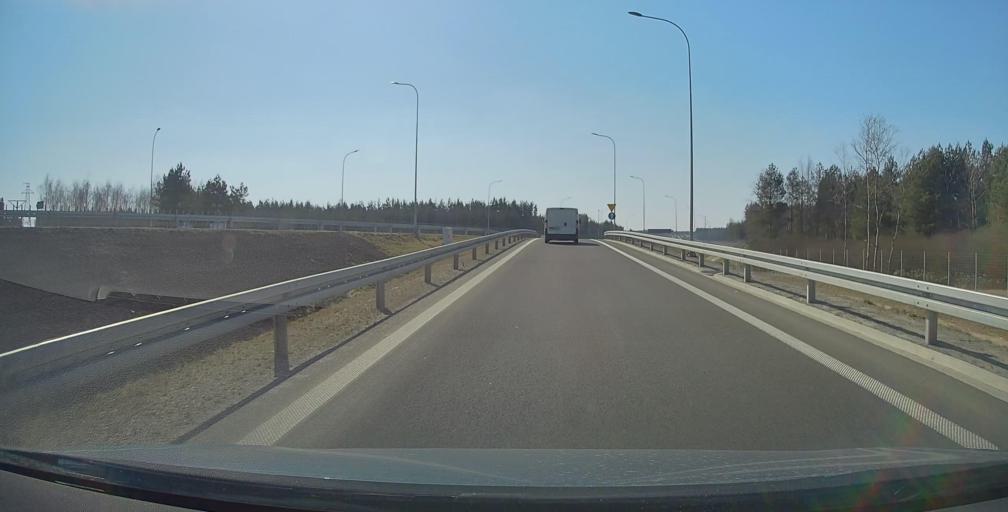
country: PL
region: Subcarpathian Voivodeship
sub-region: Powiat nizanski
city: Przedzel
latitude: 50.4944
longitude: 22.1945
